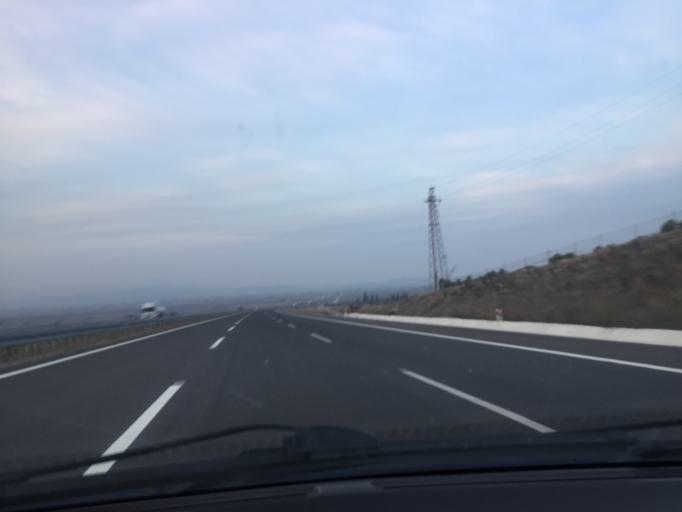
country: TR
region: Manisa
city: Halitpasa
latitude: 38.6968
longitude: 27.6425
